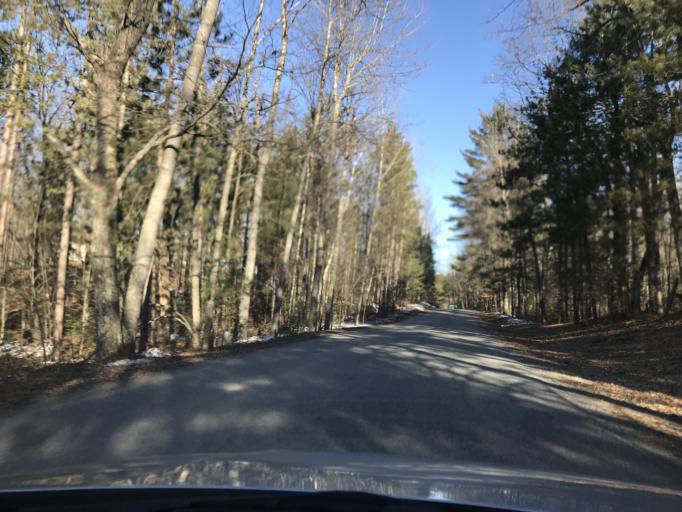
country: US
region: Wisconsin
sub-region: Marinette County
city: Niagara
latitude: 45.3909
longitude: -88.0523
